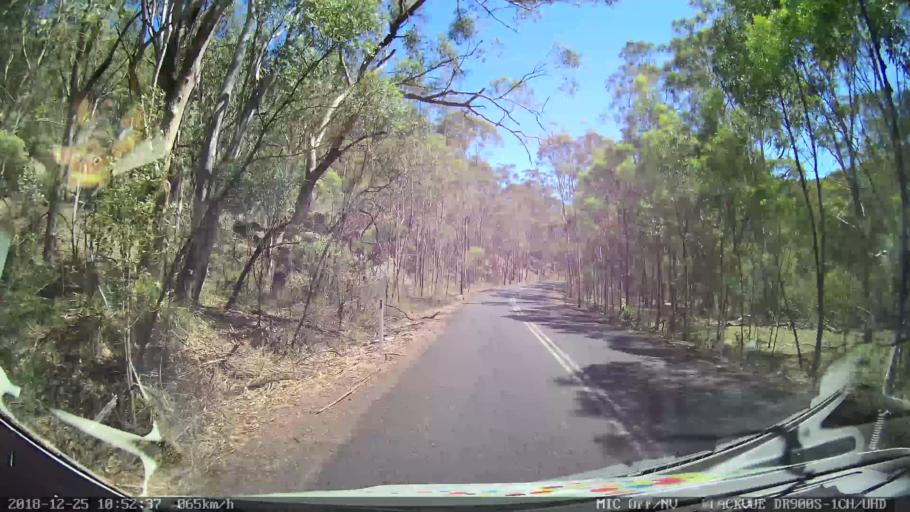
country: AU
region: New South Wales
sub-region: Upper Hunter Shire
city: Merriwa
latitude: -32.4270
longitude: 150.2733
